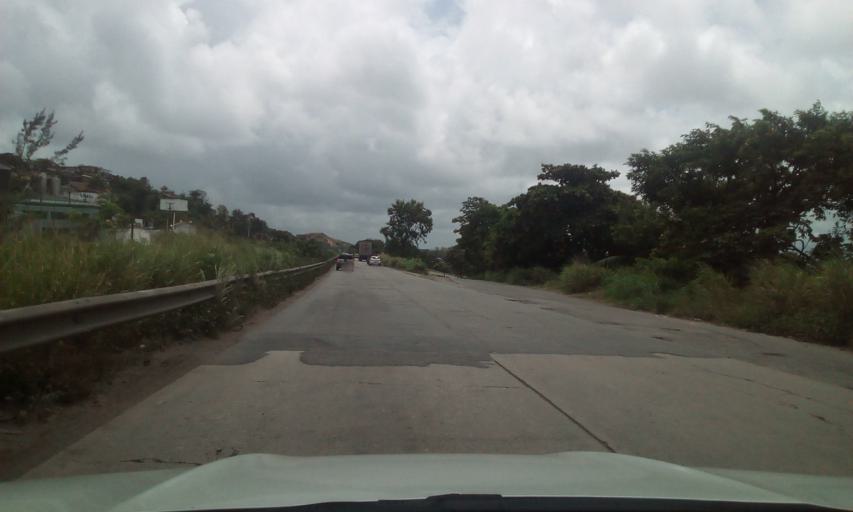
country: BR
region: Pernambuco
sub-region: Jaboatao Dos Guararapes
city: Jaboatao dos Guararapes
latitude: -8.1190
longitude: -34.9431
